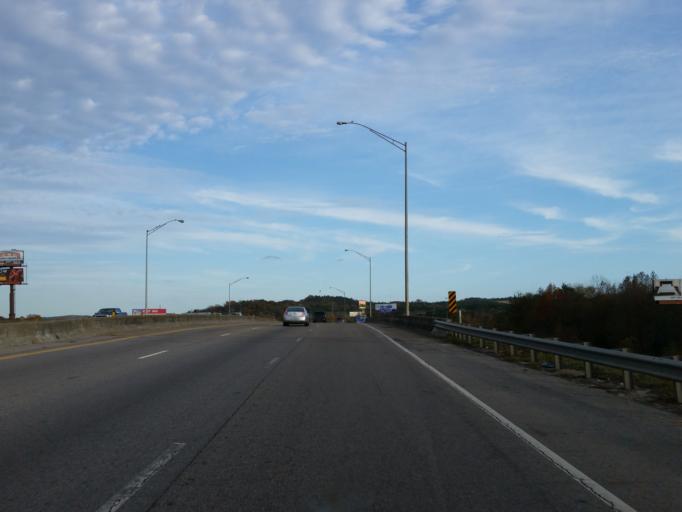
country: US
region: Mississippi
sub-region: Lauderdale County
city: Meridian
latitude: 32.3498
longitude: -88.7356
